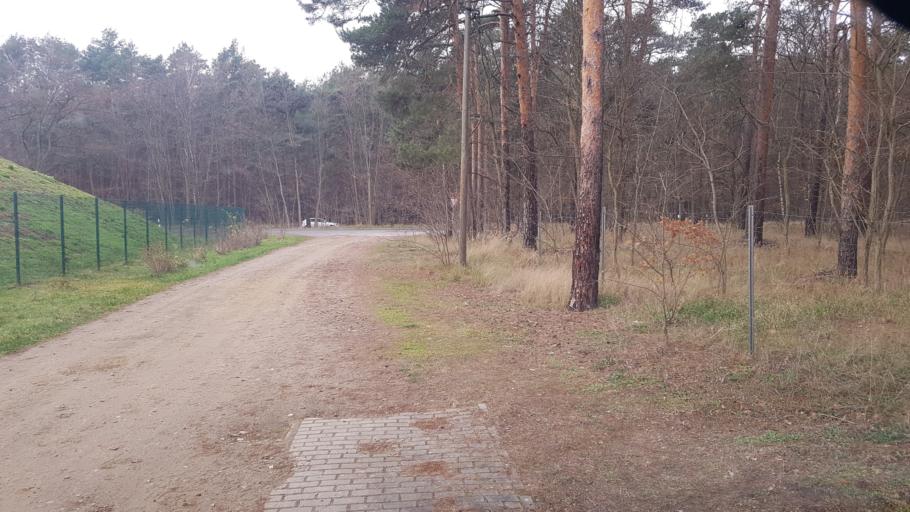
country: DE
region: Brandenburg
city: Schenkendobern
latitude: 51.9475
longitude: 14.6361
